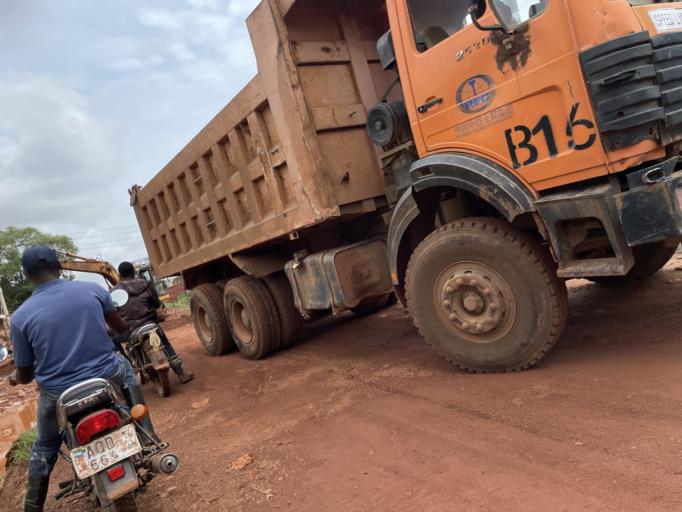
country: SL
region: Western Area
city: Hastings
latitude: 8.4152
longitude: -13.1539
